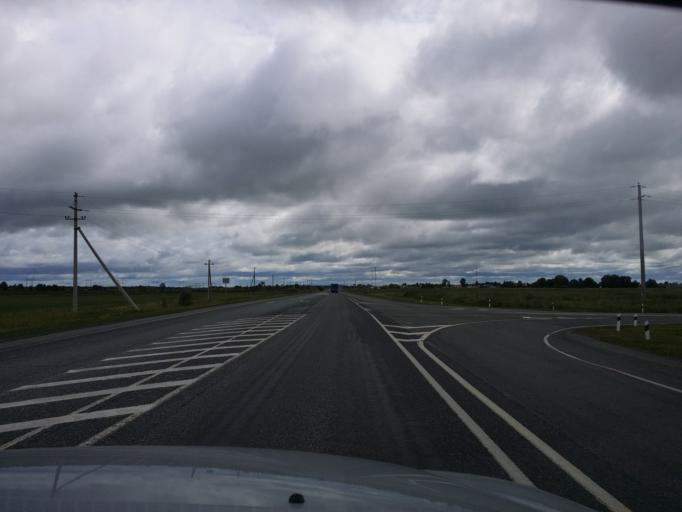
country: RU
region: Tjumen
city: Yarkovo
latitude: 57.2412
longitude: 66.7575
